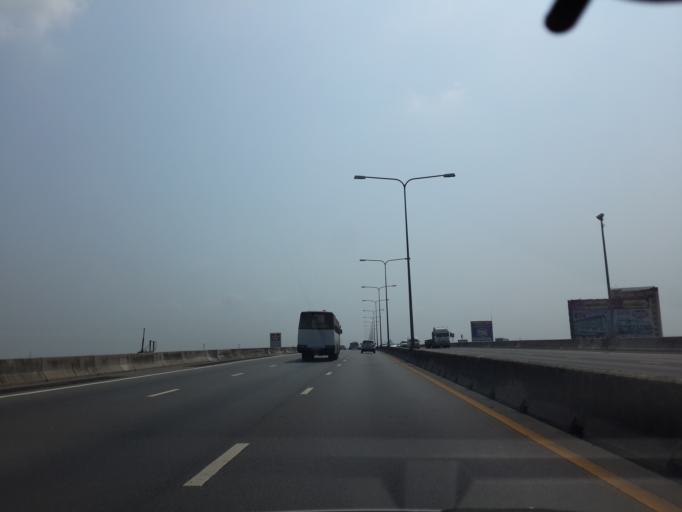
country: TH
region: Samut Prakan
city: Bang Sao Thong
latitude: 13.5883
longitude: 100.8357
